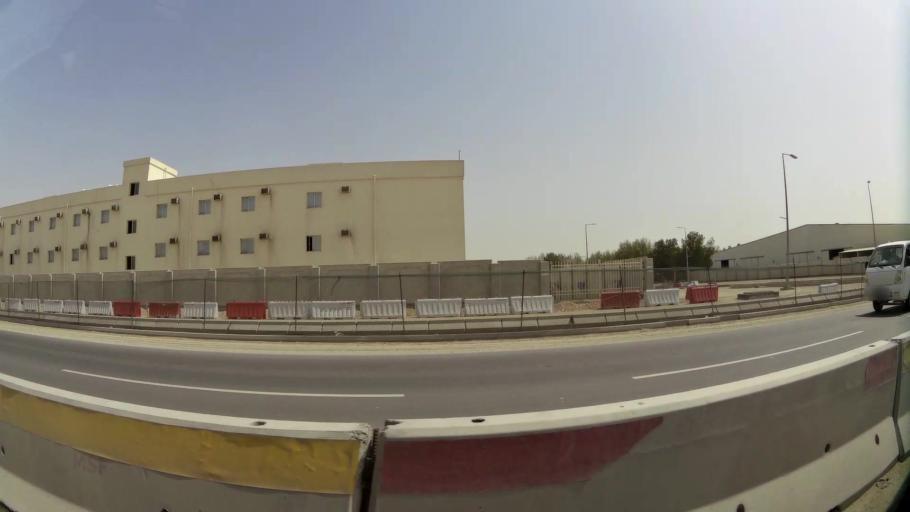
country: QA
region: Baladiyat ar Rayyan
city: Ar Rayyan
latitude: 25.1929
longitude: 51.4184
